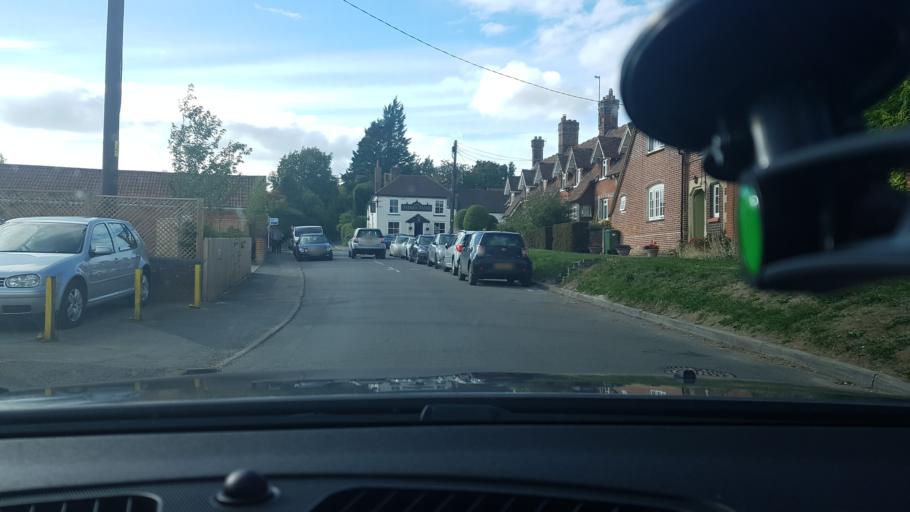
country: GB
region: England
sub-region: Wiltshire
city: Great Bedwyn
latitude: 51.3797
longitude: -1.6026
